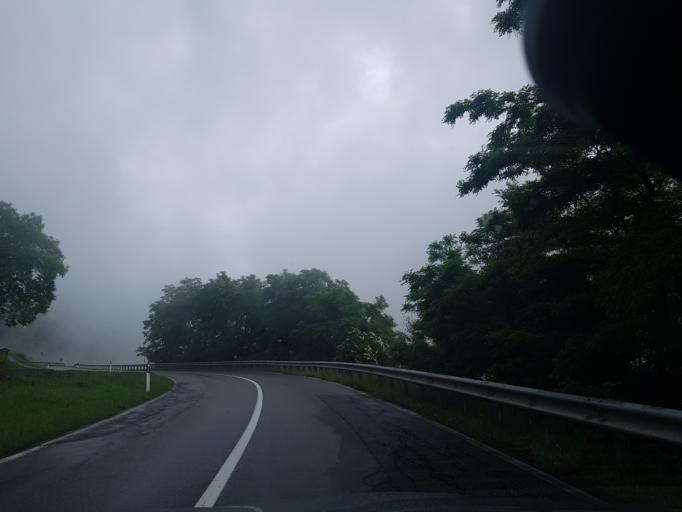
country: IT
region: Trentino-Alto Adige
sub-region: Bolzano
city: Laion
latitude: 46.5980
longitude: 11.6160
